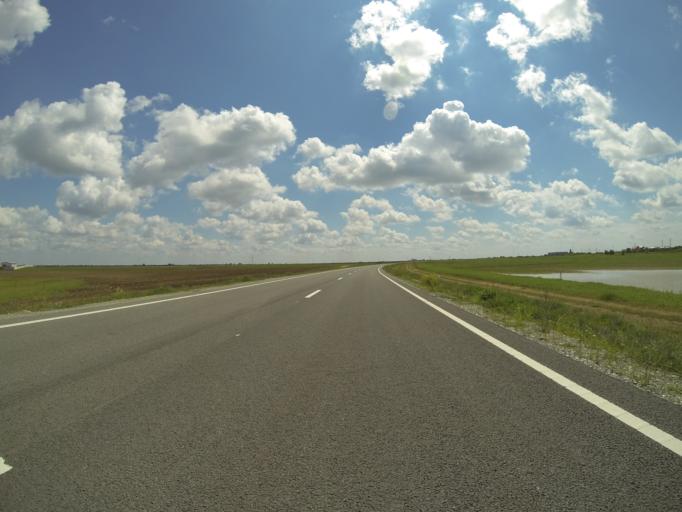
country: RO
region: Dolj
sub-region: Comuna Carcea
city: Carcea
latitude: 44.2686
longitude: 23.9119
